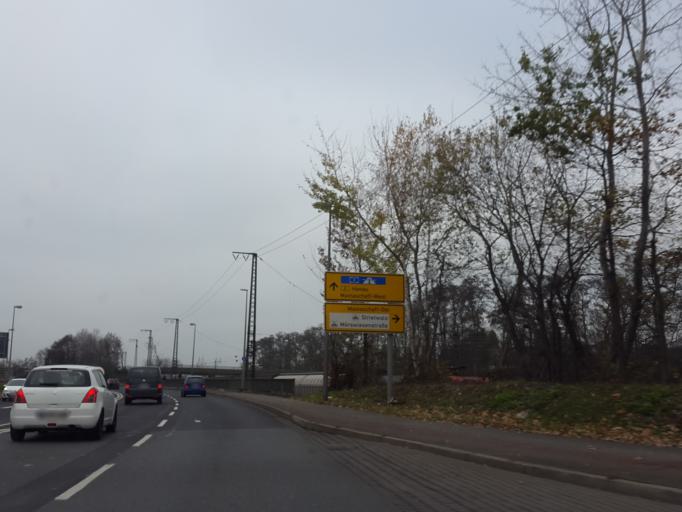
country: DE
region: Bavaria
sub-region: Regierungsbezirk Unterfranken
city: Aschaffenburg
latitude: 49.9809
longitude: 9.1235
